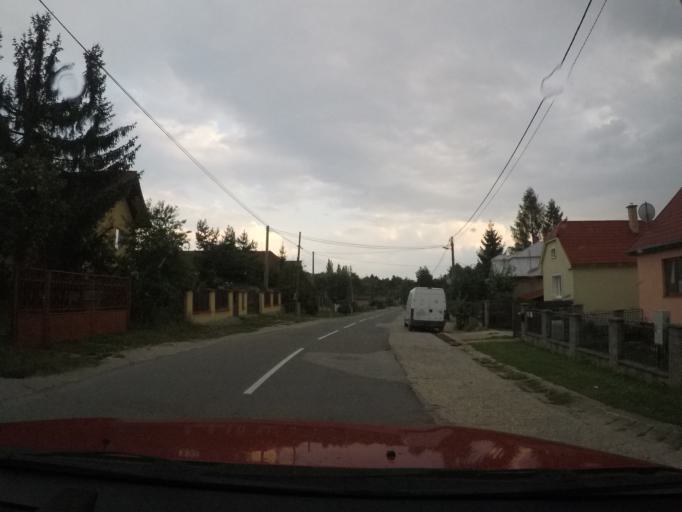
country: SK
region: Kosicky
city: Kosice
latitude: 48.6887
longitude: 21.1942
